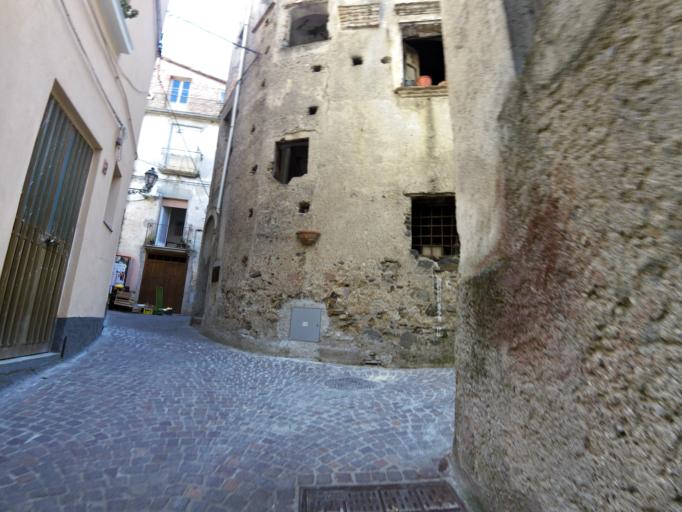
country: IT
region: Calabria
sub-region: Provincia di Reggio Calabria
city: Bivongi
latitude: 38.4834
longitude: 16.4529
